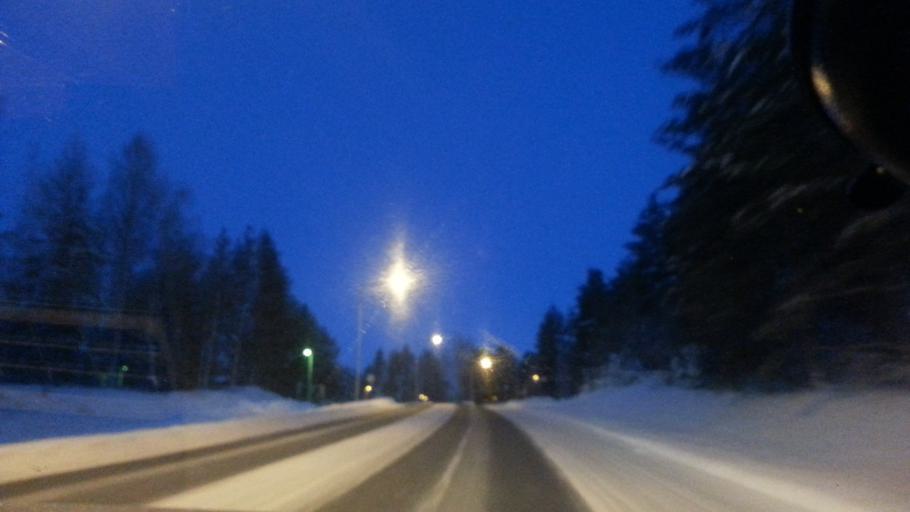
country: FI
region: Lapland
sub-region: Rovaniemi
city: Rovaniemi
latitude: 66.4933
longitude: 25.7573
